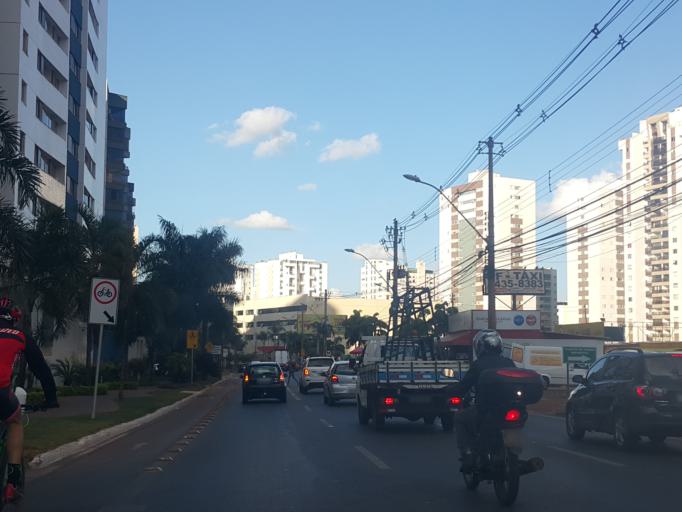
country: BR
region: Federal District
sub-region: Brasilia
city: Brasilia
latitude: -15.8416
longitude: -48.0268
